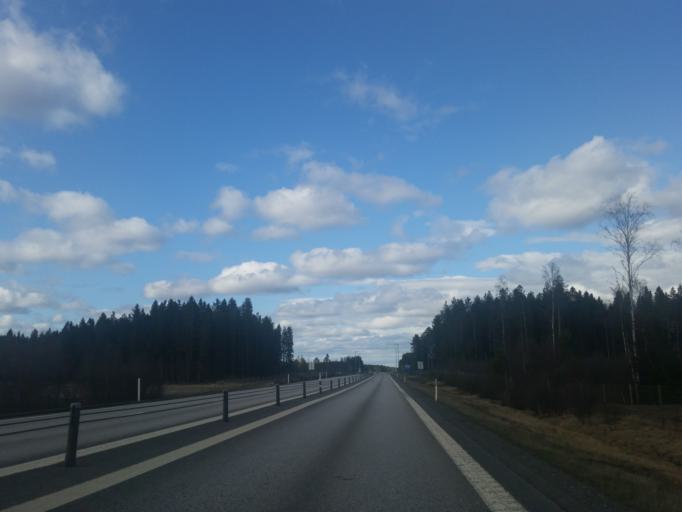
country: SE
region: Vaesterbotten
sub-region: Robertsfors Kommun
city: Robertsfors
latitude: 64.0870
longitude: 20.8687
